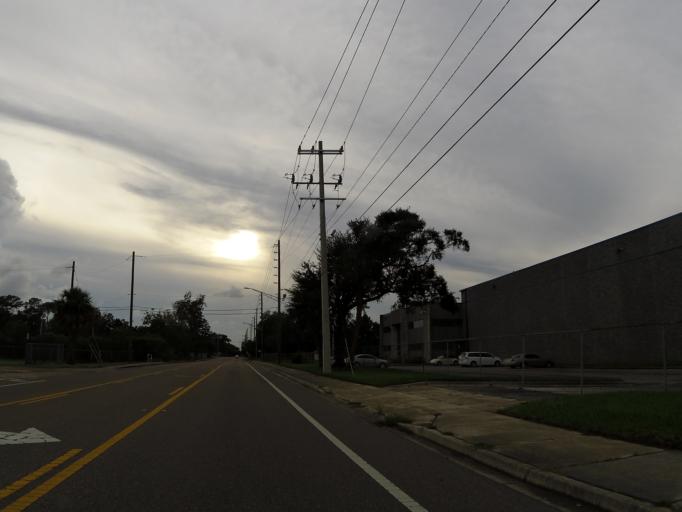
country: US
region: Florida
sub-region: Duval County
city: Jacksonville
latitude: 30.3440
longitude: -81.7087
